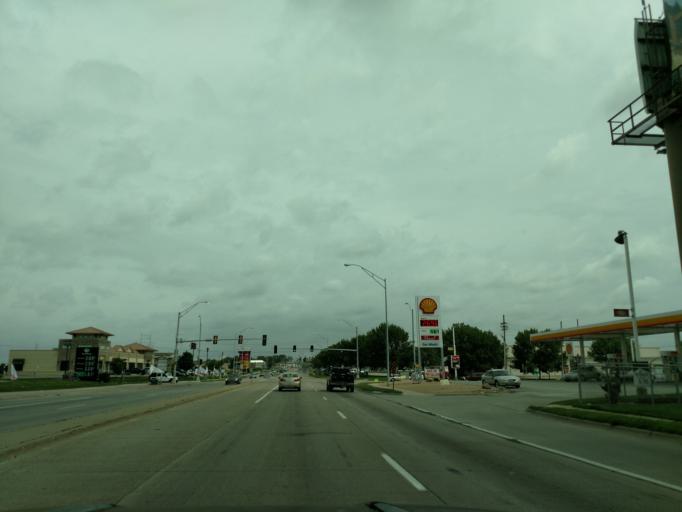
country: US
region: Nebraska
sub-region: Douglas County
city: Ralston
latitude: 41.2044
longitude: -96.0238
